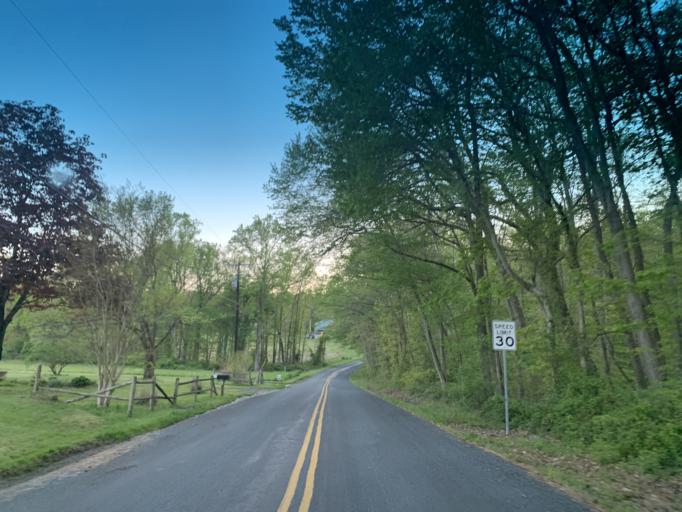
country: US
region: Maryland
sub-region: Harford County
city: Riverside
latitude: 39.5298
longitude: -76.2300
